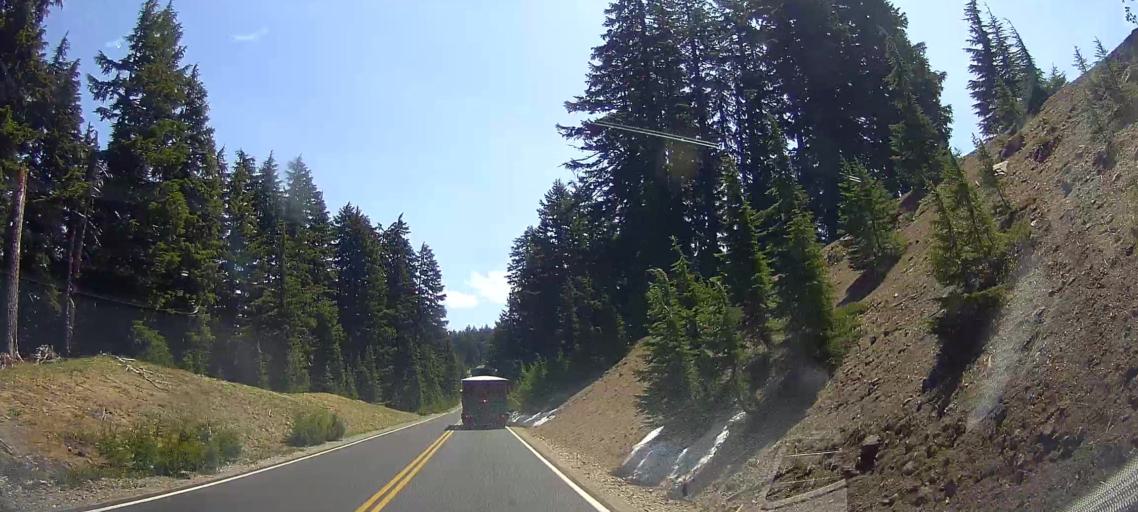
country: US
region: Oregon
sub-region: Jackson County
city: Shady Cove
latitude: 42.9799
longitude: -122.1193
